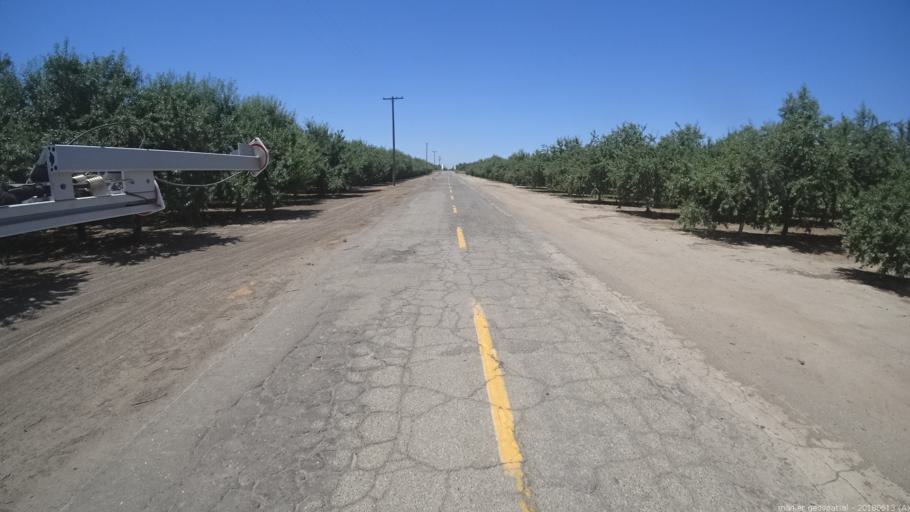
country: US
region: California
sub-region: Madera County
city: Chowchilla
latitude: 37.0615
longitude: -120.2757
